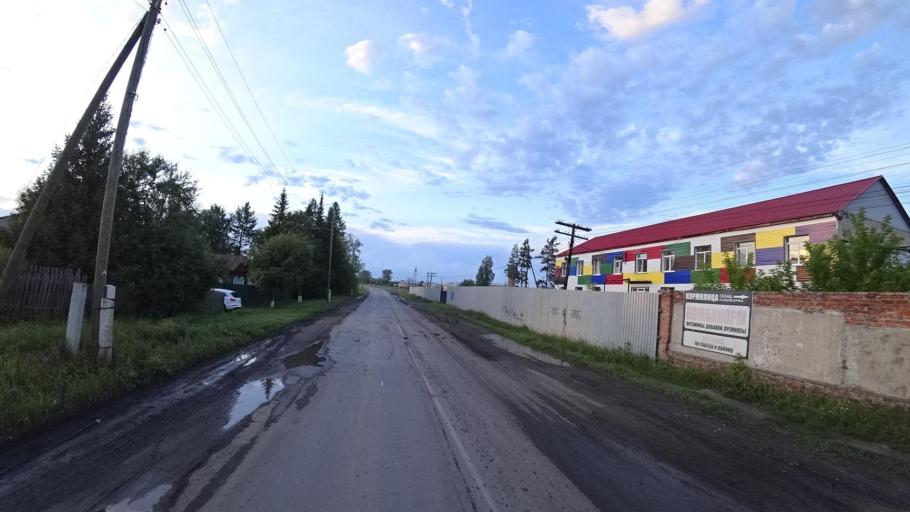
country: RU
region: Sverdlovsk
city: Kamyshlov
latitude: 56.8641
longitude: 62.7098
